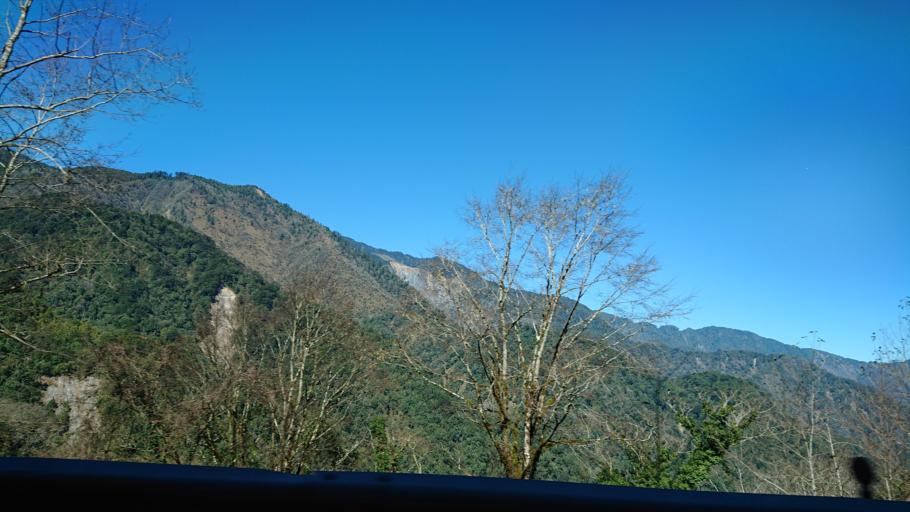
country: TW
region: Taiwan
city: Daxi
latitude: 24.4015
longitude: 121.3637
